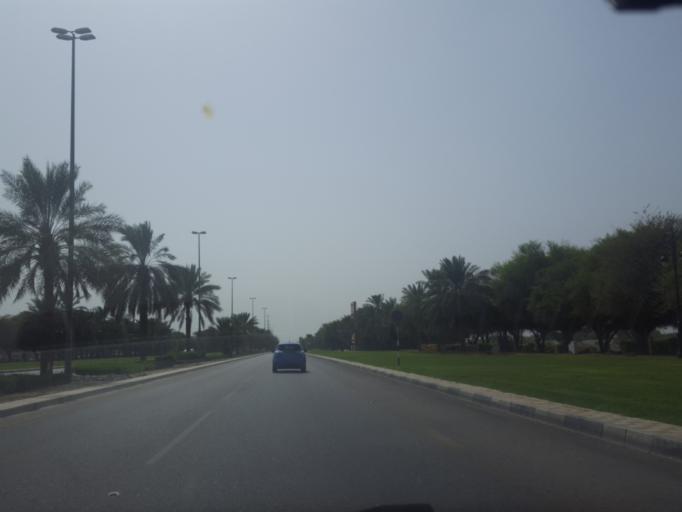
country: AE
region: Abu Dhabi
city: Al Ain
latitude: 24.2056
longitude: 55.7970
